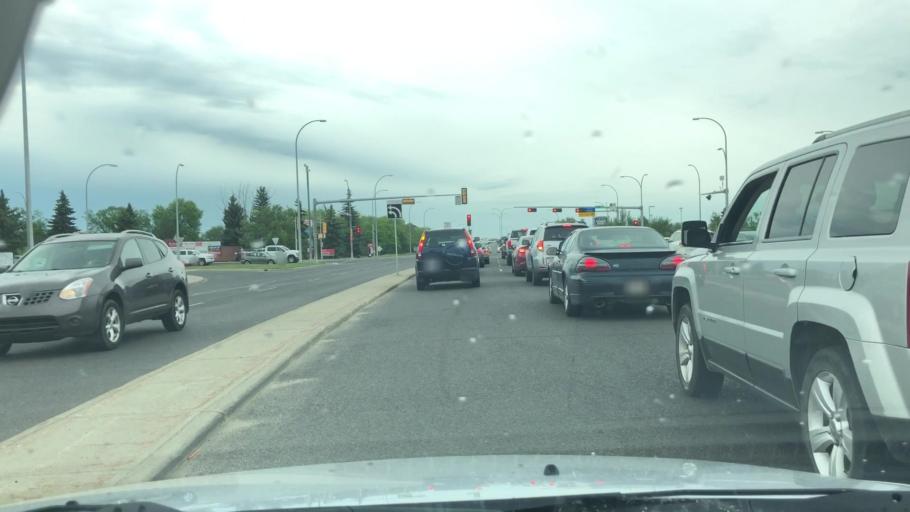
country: CA
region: Alberta
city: Edmonton
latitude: 53.5986
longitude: -113.4920
